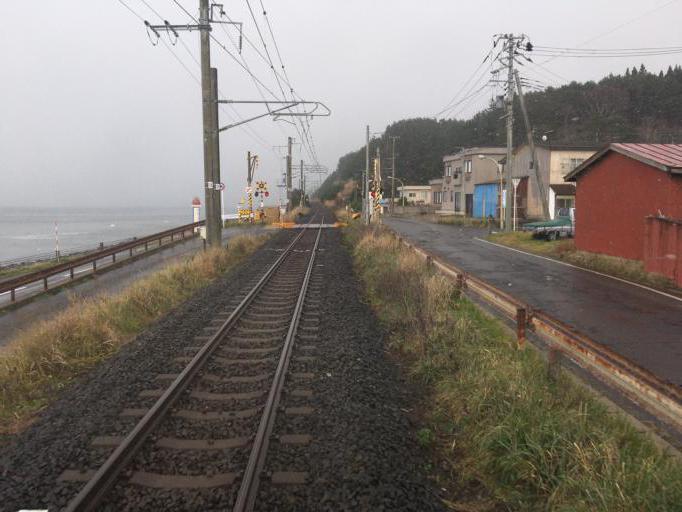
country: JP
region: Aomori
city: Aomori Shi
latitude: 41.0338
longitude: 140.6458
